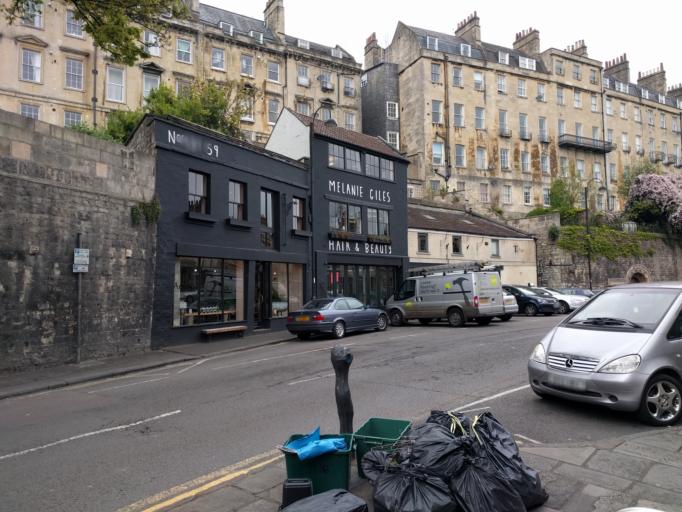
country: GB
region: England
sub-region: Bath and North East Somerset
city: Bath
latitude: 51.3856
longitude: -2.3597
